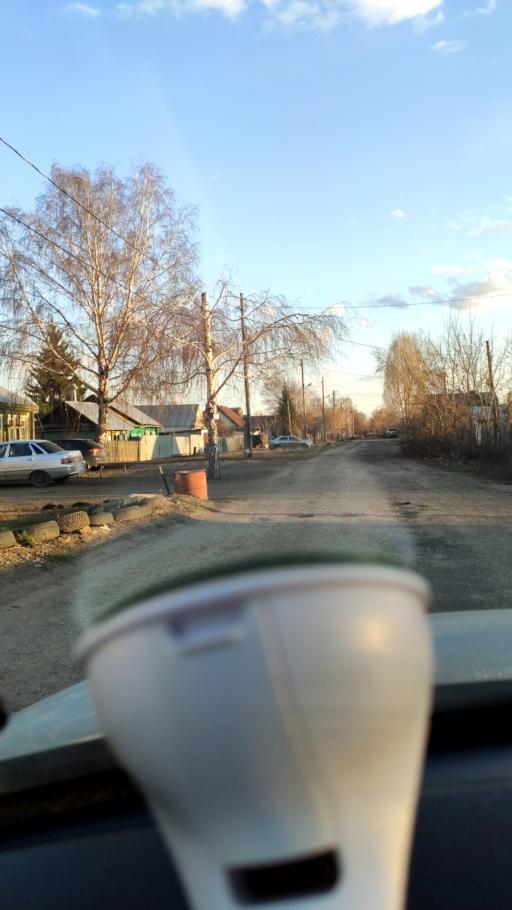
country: RU
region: Samara
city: Smyshlyayevka
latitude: 53.2488
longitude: 50.3429
